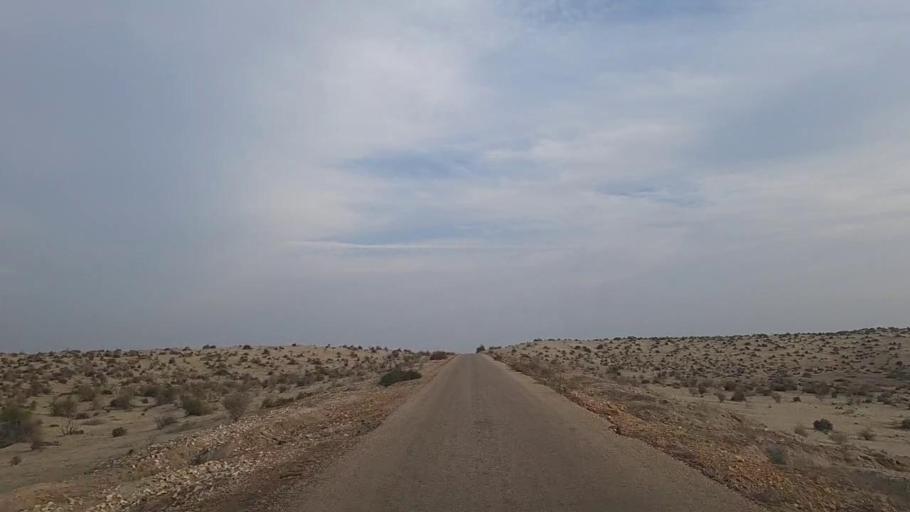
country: PK
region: Sindh
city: Daur
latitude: 26.5095
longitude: 68.5095
